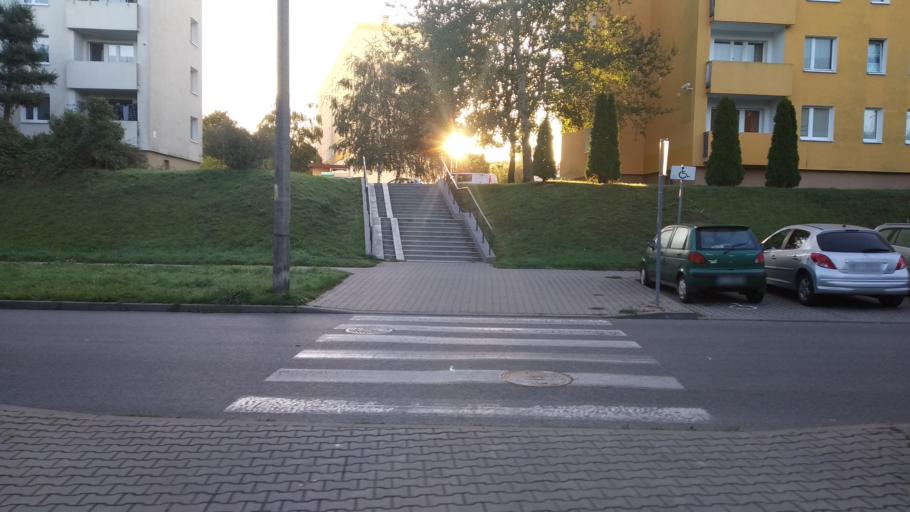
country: PL
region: Lubusz
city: Gorzow Wielkopolski
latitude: 52.7529
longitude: 15.2262
